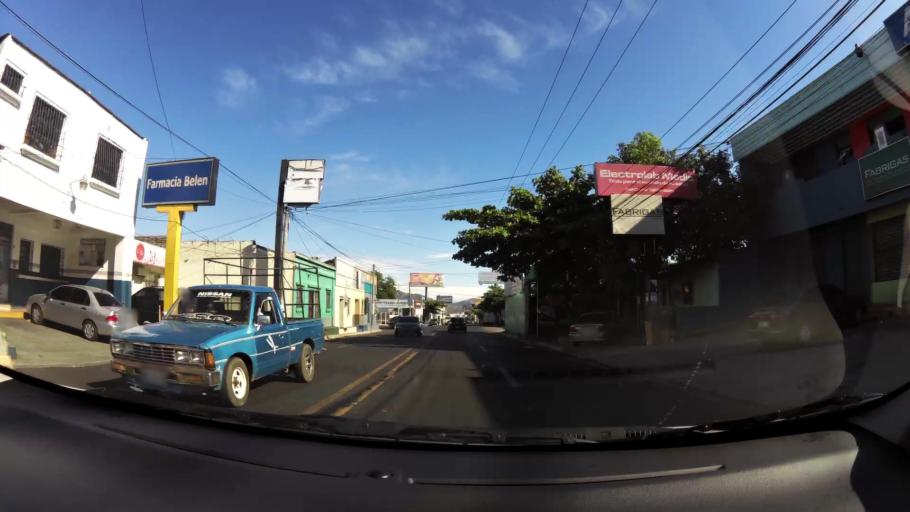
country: SV
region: Santa Ana
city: Santa Ana
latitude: 13.9795
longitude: -89.5601
